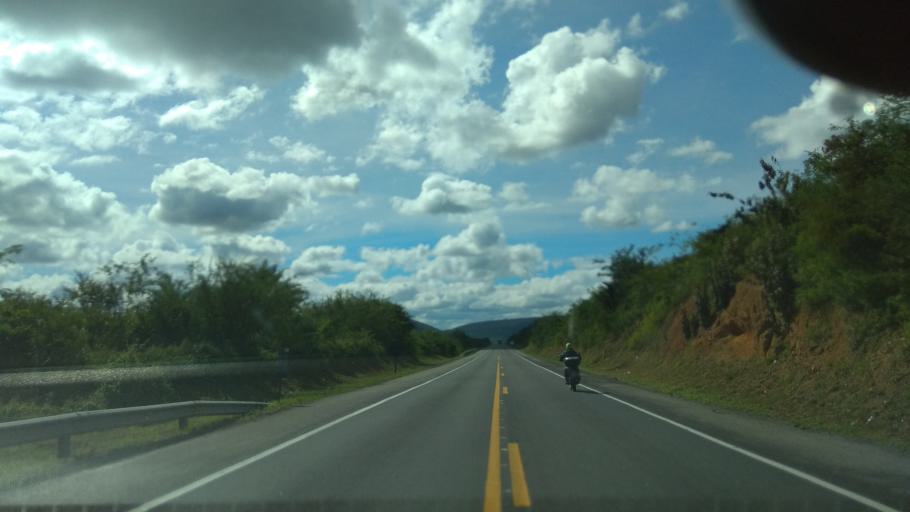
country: BR
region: Bahia
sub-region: Santa Ines
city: Santa Ines
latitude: -13.3036
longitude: -40.0258
